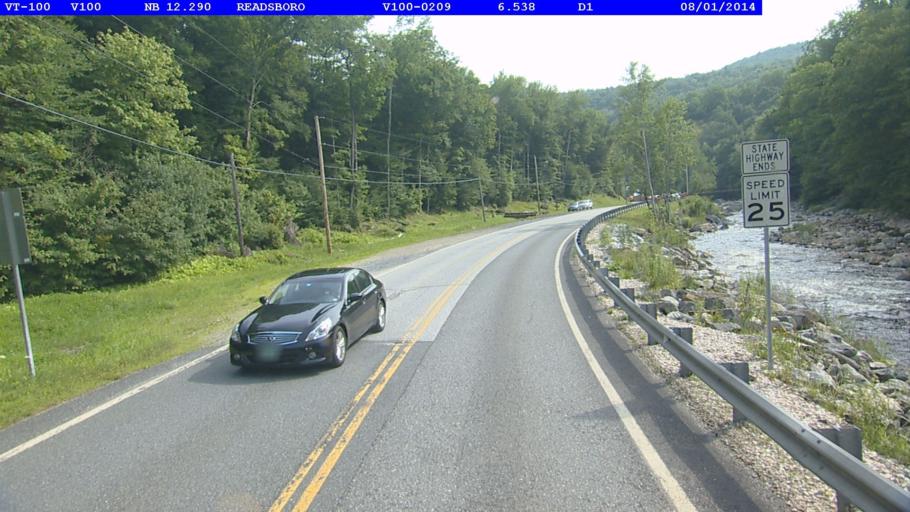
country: US
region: Massachusetts
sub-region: Franklin County
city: Charlemont
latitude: 42.7769
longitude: -72.9517
